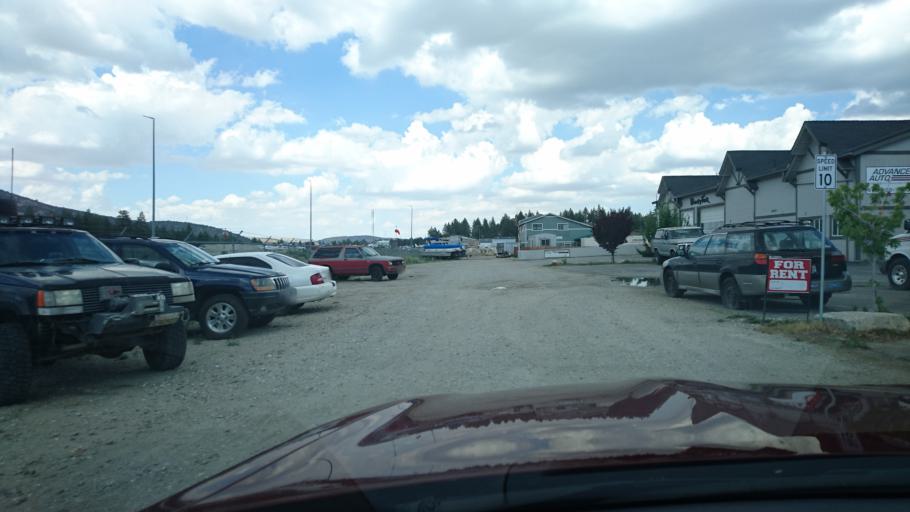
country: US
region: California
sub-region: San Bernardino County
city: Big Bear City
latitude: 34.2624
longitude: -116.8566
